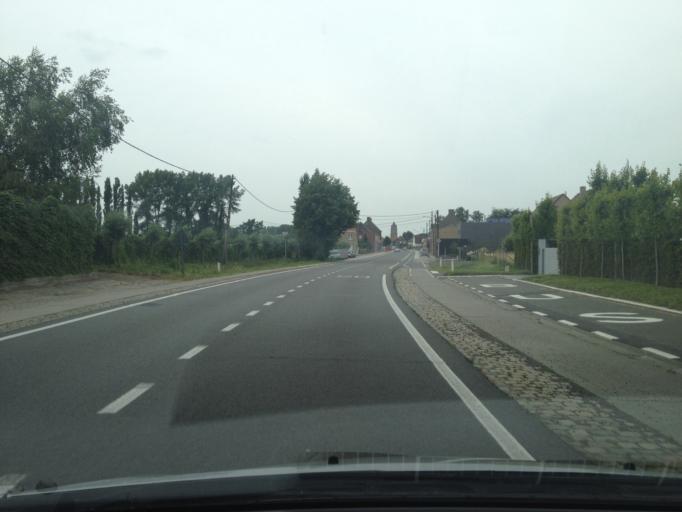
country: BE
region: Flanders
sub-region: Provincie West-Vlaanderen
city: Diksmuide
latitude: 50.9918
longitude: 2.8702
